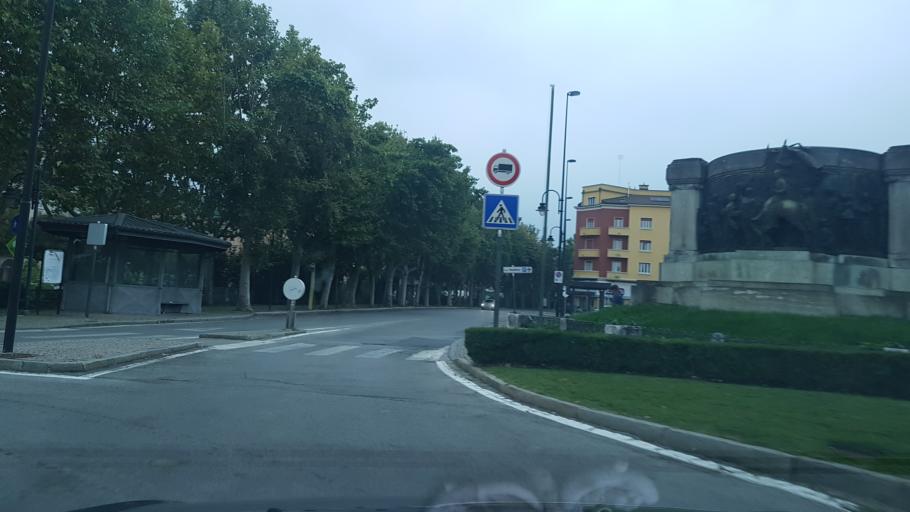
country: IT
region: Piedmont
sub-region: Provincia di Cuneo
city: Mondovi
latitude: 44.3901
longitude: 7.8195
